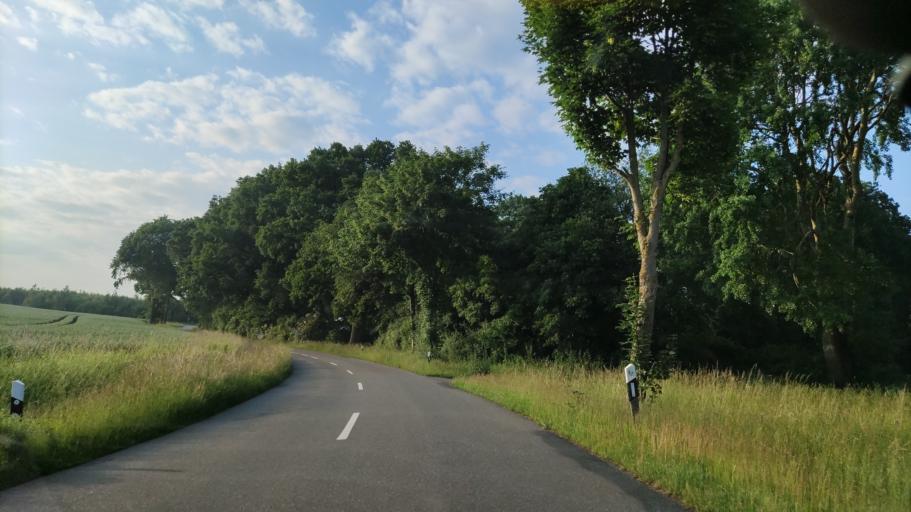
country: DE
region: Lower Saxony
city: Hanstedt Eins
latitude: 53.0400
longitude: 10.3487
